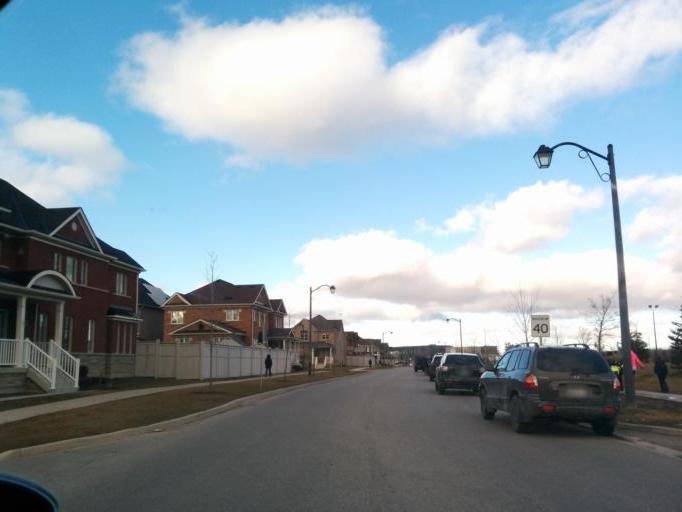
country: CA
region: Ontario
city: Bradford West Gwillimbury
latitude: 44.1016
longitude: -79.5875
